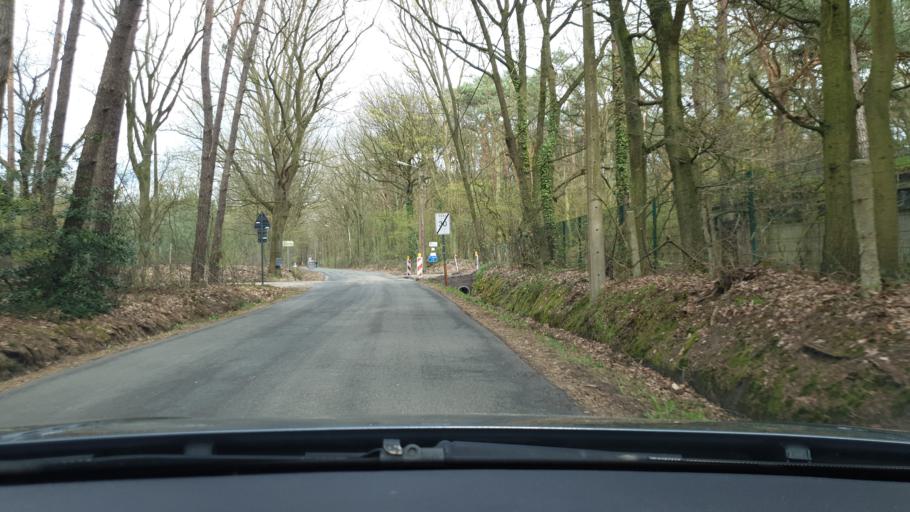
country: BE
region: Flanders
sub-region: Provincie Limburg
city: Zonhoven
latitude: 50.9532
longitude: 5.3749
